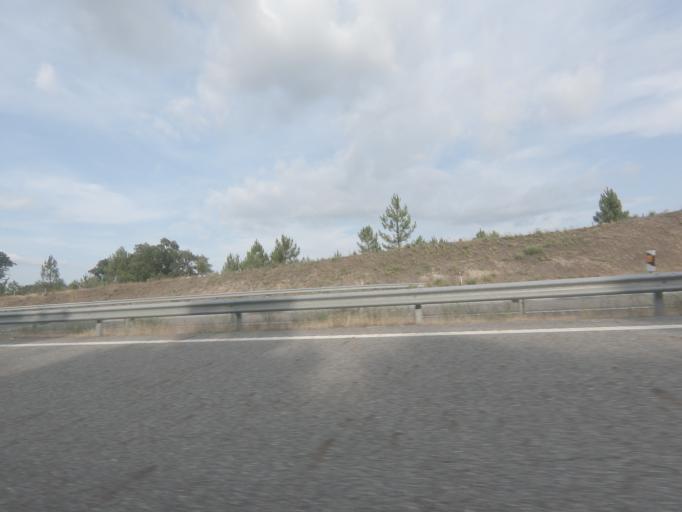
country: PT
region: Vila Real
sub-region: Chaves
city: Chaves
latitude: 41.6945
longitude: -7.5543
